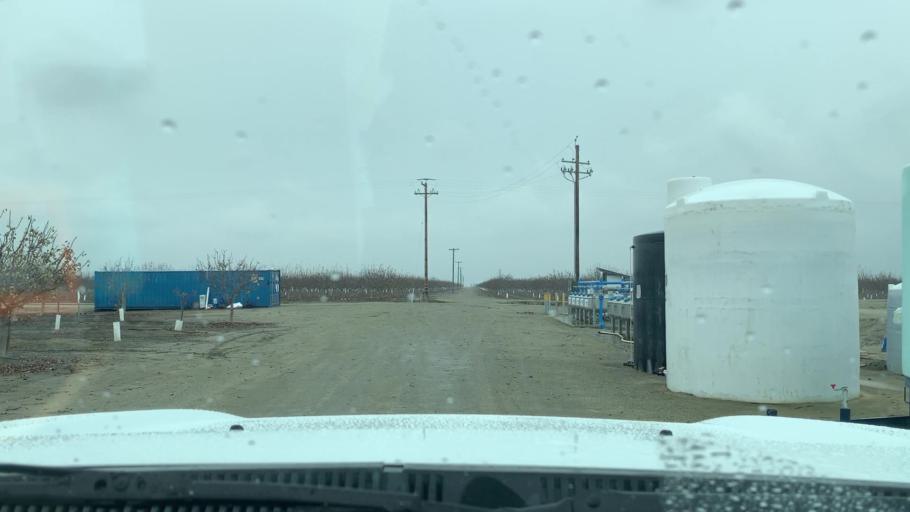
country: US
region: California
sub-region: Kings County
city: Corcoran
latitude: 36.0290
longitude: -119.4923
